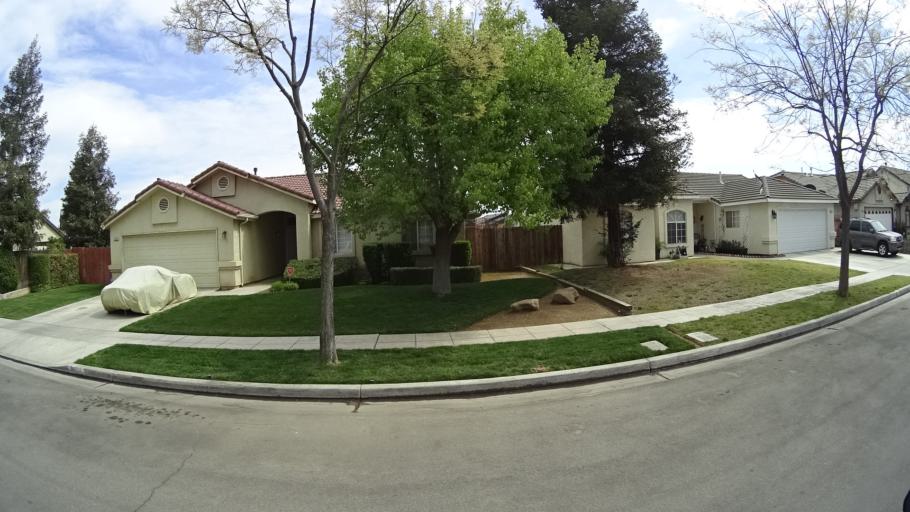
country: US
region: California
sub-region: Fresno County
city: West Park
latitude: 36.8183
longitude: -119.8854
